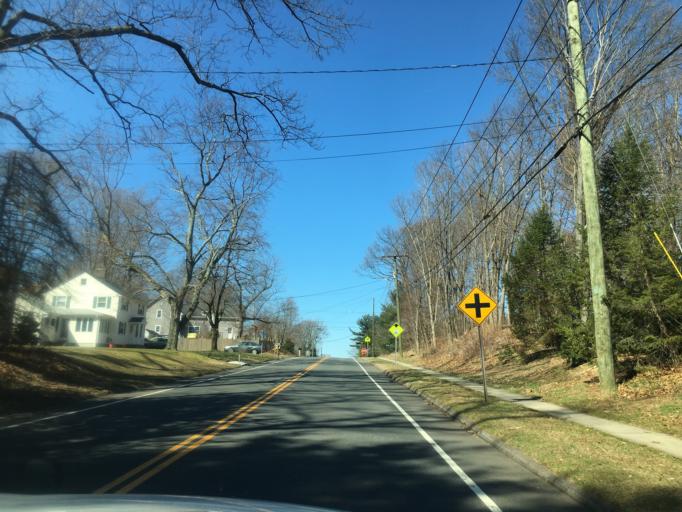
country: US
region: Connecticut
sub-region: Hartford County
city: East Hartford
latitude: 41.8055
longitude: -72.5921
